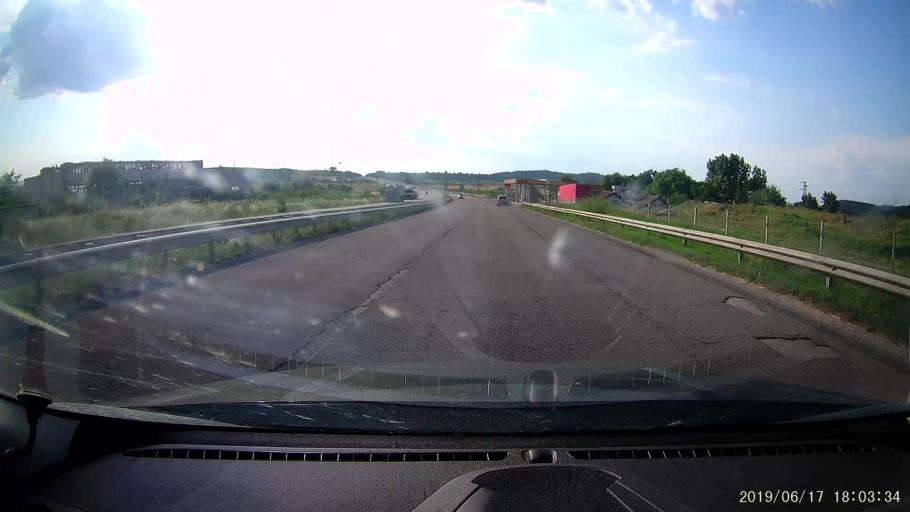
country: BG
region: Khaskovo
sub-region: Obshtina Svilengrad
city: Svilengrad
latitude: 41.7793
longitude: 26.2168
